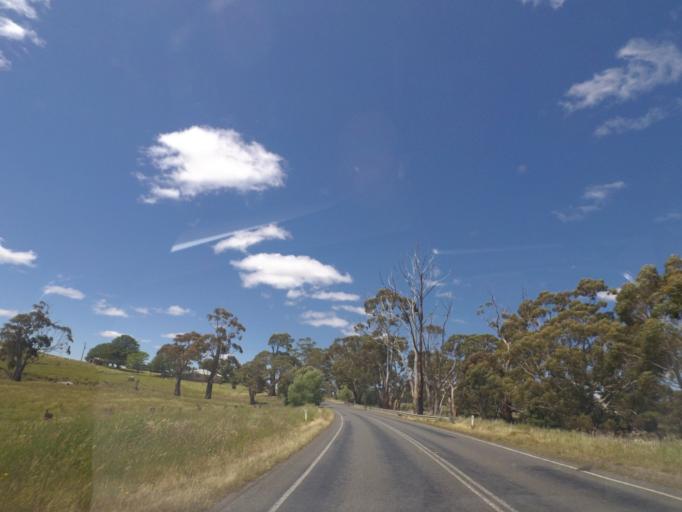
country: AU
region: Victoria
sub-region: Mount Alexander
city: Castlemaine
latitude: -37.3147
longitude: 144.2247
